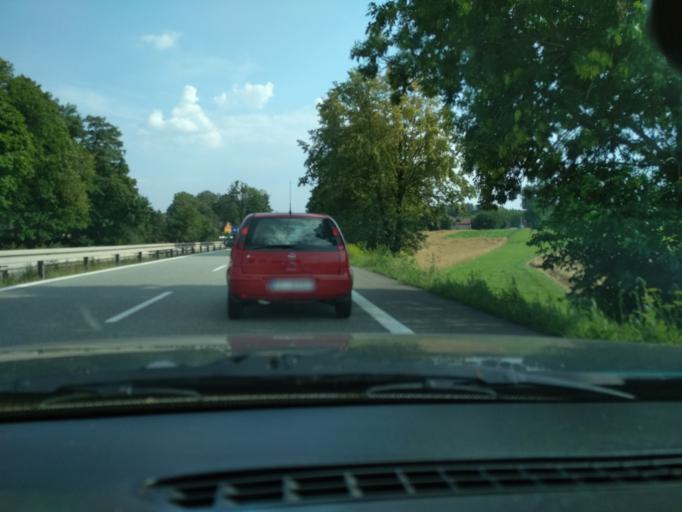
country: PL
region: Silesian Voivodeship
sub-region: Powiat pszczynski
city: Pawlowice
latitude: 49.9996
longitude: 18.7112
